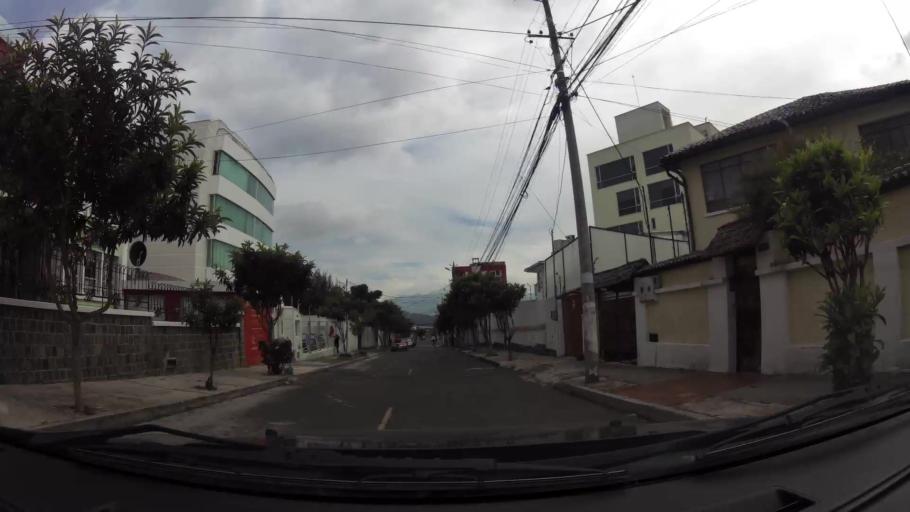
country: EC
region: Pichincha
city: Quito
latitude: -0.2082
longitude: -78.4815
